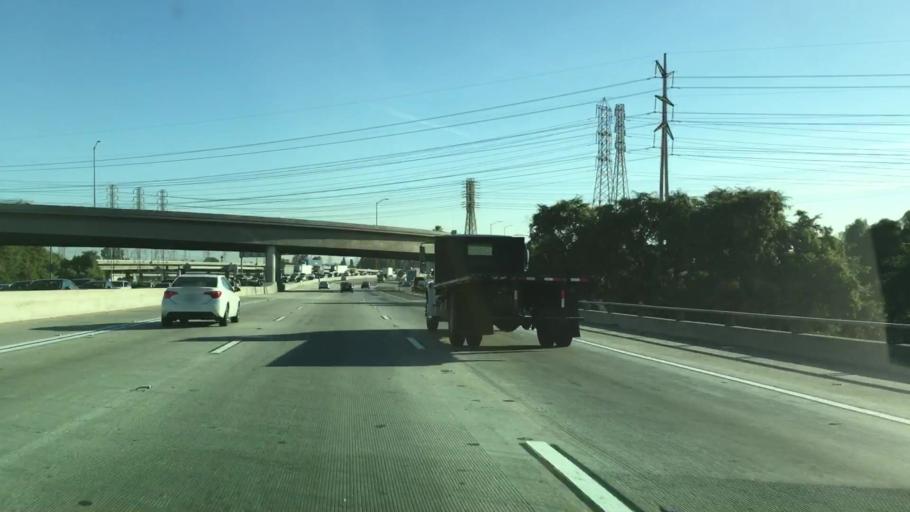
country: US
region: California
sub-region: Los Angeles County
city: East Rancho Dominguez
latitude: 33.8728
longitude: -118.1998
